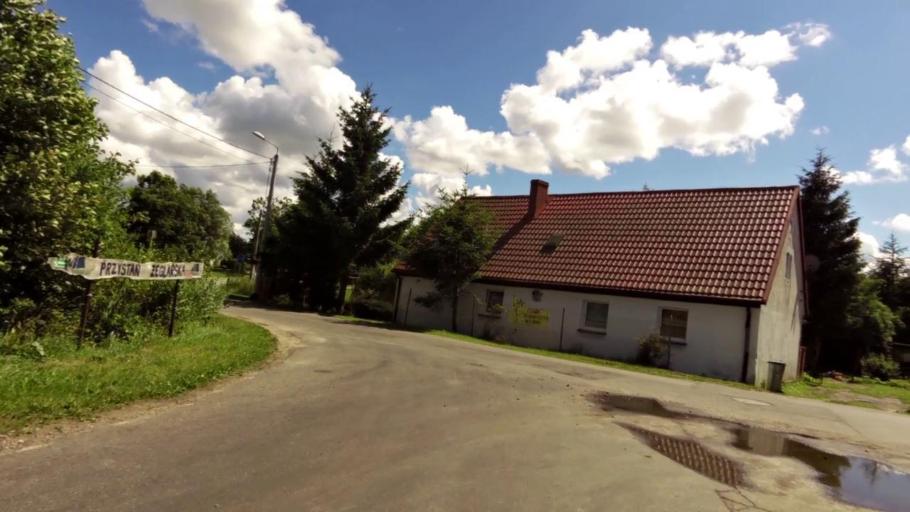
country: PL
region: West Pomeranian Voivodeship
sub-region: Powiat slawienski
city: Slawno
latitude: 54.5239
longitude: 16.6080
